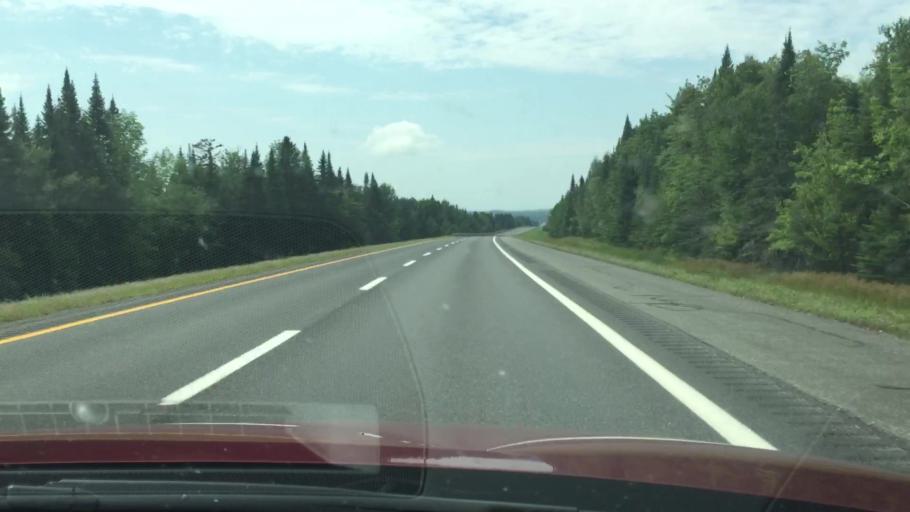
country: US
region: Maine
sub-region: Aroostook County
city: Hodgdon
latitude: 46.1201
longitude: -68.1193
